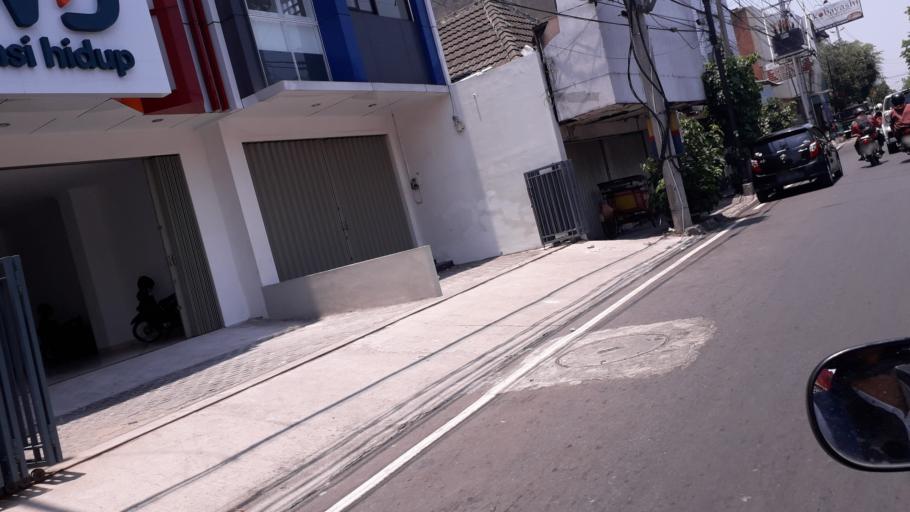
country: ID
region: Daerah Istimewa Yogyakarta
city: Yogyakarta
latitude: -7.7786
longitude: 110.3610
